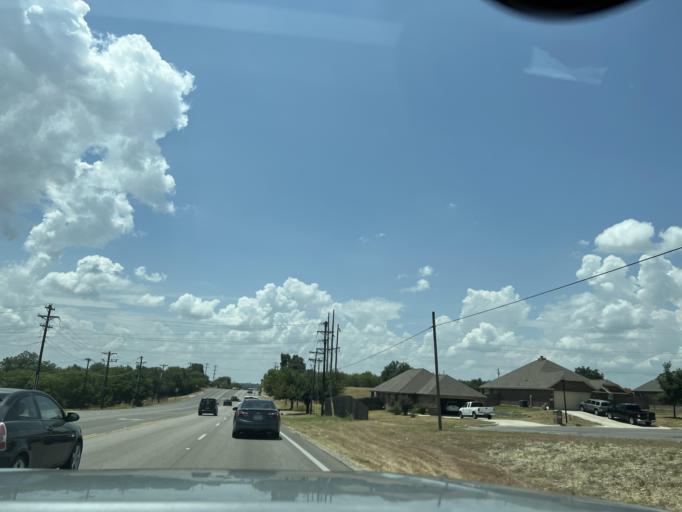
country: US
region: Texas
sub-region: Parker County
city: Weatherford
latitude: 32.7821
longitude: -97.7974
